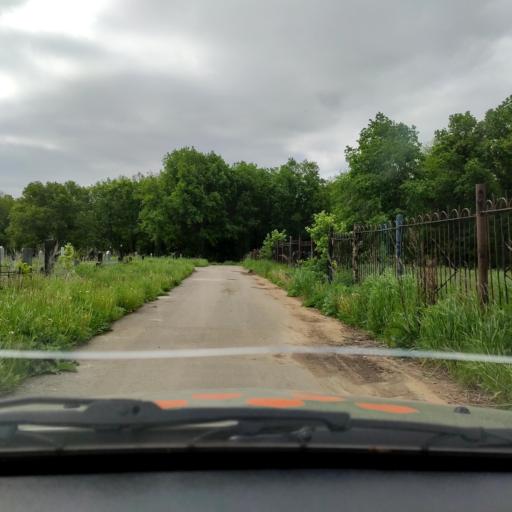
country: RU
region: Bashkortostan
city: Mikhaylovka
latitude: 54.8118
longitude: 55.8571
